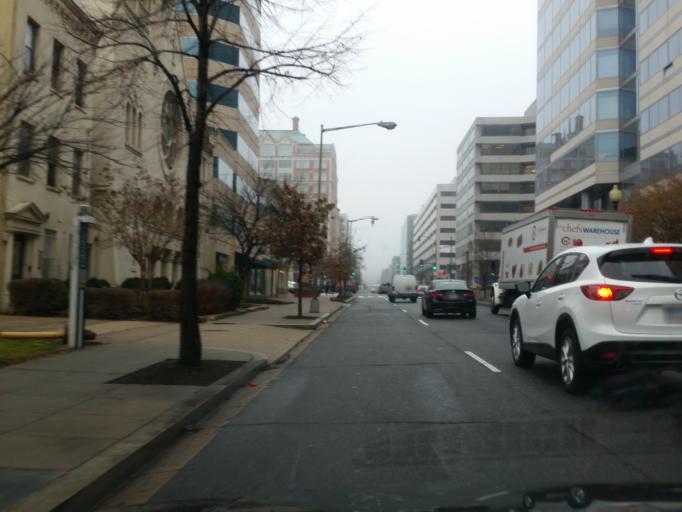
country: US
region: Washington, D.C.
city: Washington, D.C.
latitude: 38.8998
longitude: -77.0449
